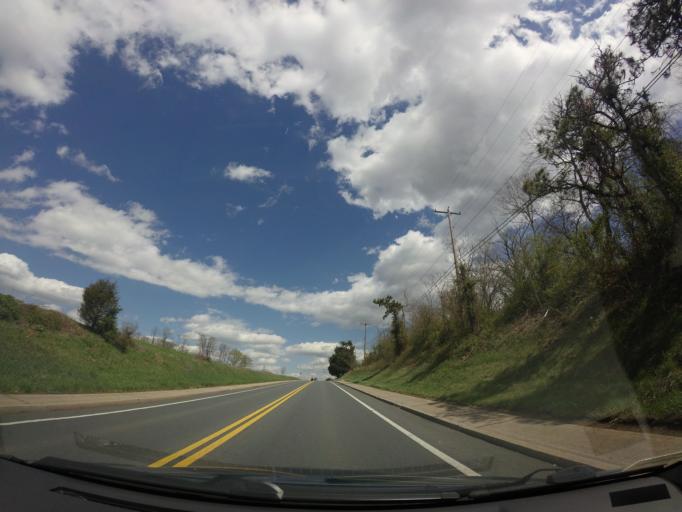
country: US
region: West Virginia
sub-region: Jefferson County
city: Shepherdstown
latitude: 39.4458
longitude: -77.7750
